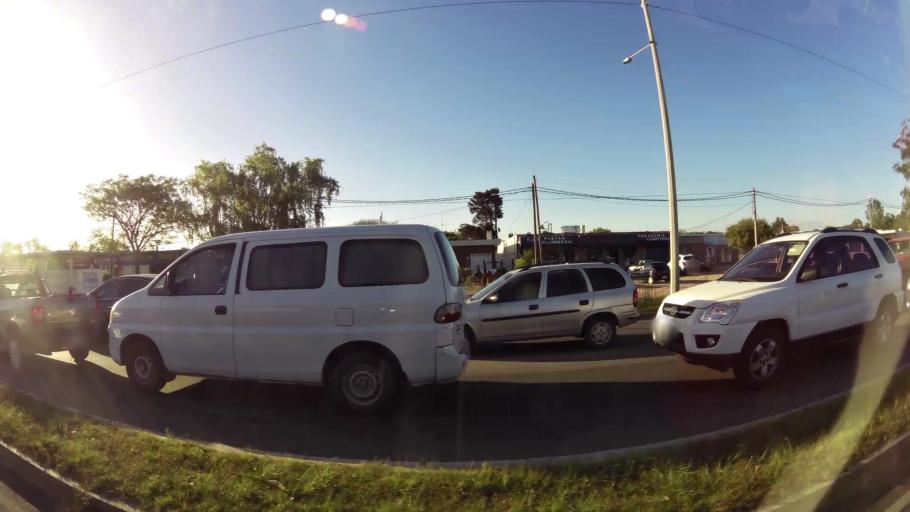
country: UY
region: Canelones
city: Paso de Carrasco
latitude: -34.8565
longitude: -56.0452
